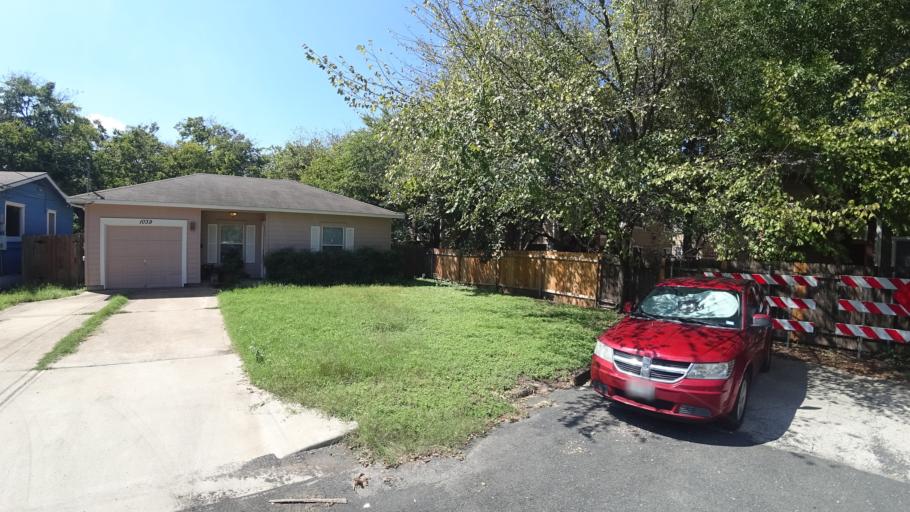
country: US
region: Texas
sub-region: Travis County
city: Austin
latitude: 30.3196
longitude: -97.7025
